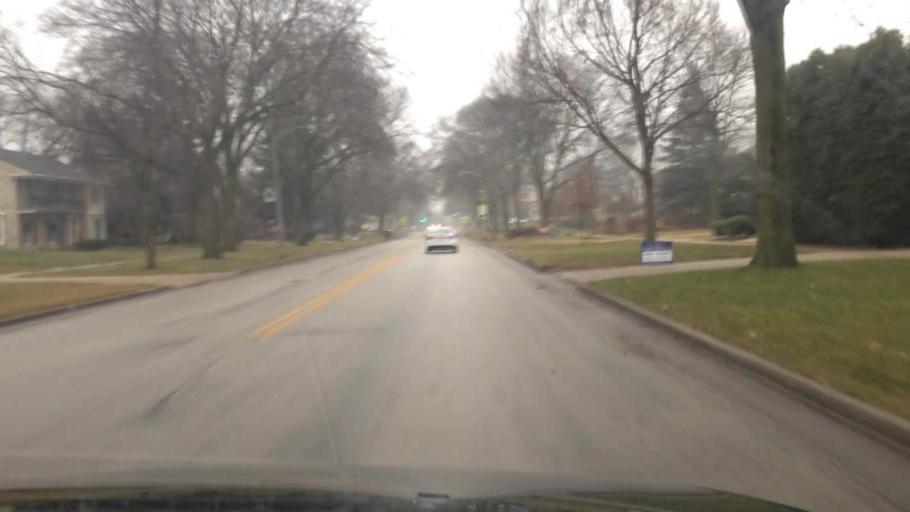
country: US
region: Wisconsin
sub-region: Milwaukee County
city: Wauwatosa
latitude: 43.0641
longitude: -88.0276
